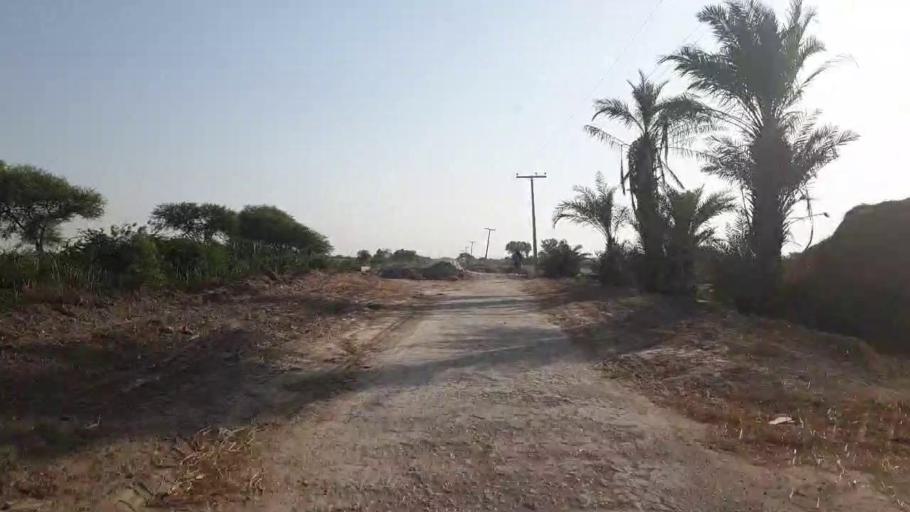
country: PK
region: Sindh
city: Talhar
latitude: 24.9147
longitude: 68.7442
